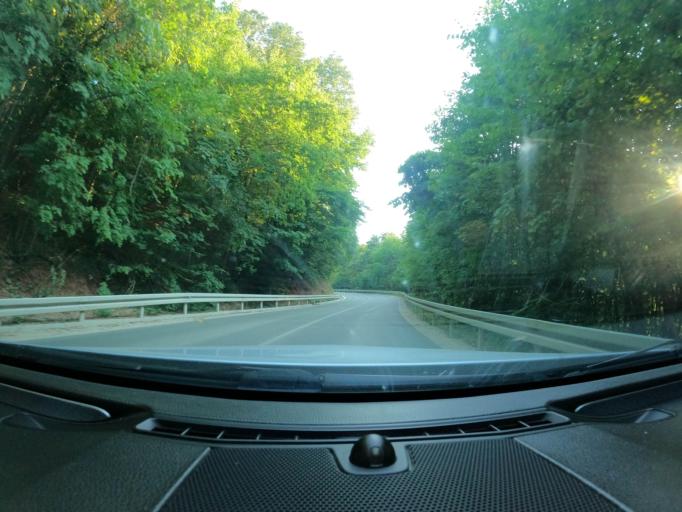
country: RS
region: Autonomna Pokrajina Vojvodina
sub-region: Juznobacki Okrug
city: Beocin
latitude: 45.1615
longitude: 19.7147
